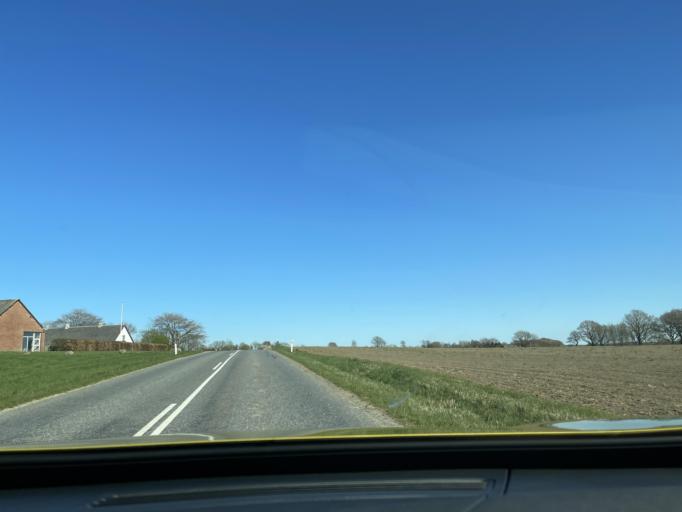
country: DK
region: Central Jutland
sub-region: Silkeborg Kommune
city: Kjellerup
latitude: 56.2587
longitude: 9.4024
